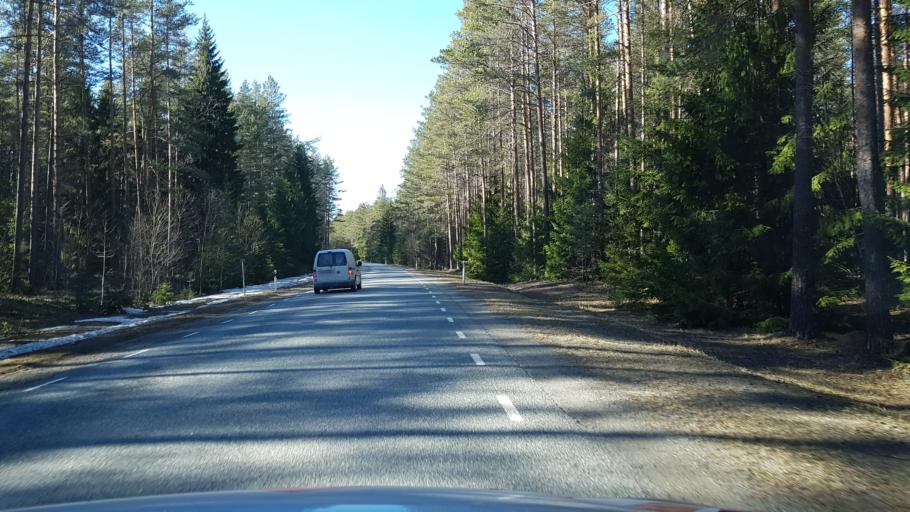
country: EE
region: Laeaene-Virumaa
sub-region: Vinni vald
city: Vinni
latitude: 59.2609
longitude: 26.6817
